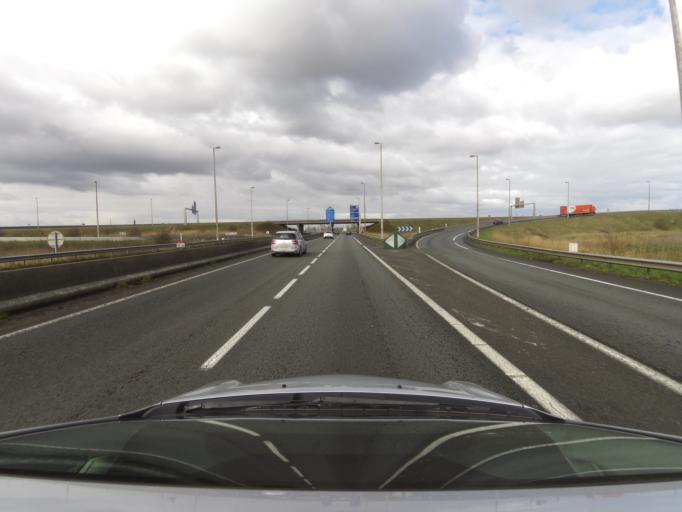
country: FR
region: Nord-Pas-de-Calais
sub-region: Departement du Pas-de-Calais
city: Coulogne
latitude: 50.9361
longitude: 1.9097
